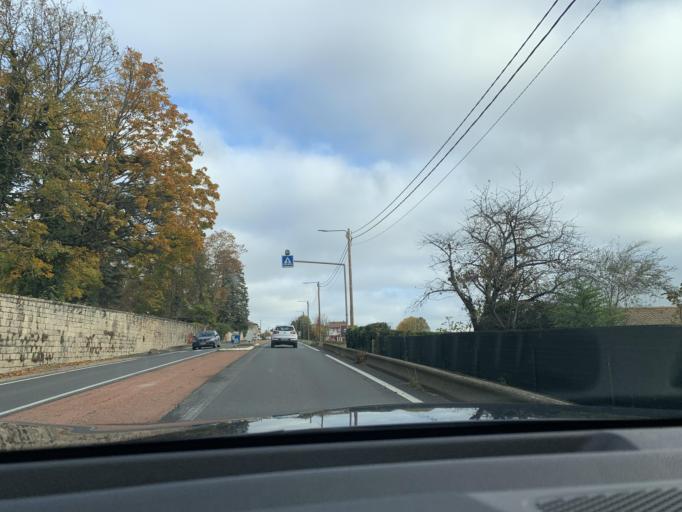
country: FR
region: Bourgogne
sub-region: Departement de Saone-et-Loire
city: Saint-Martin-Belle-Roche
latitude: 46.3630
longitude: 4.8516
